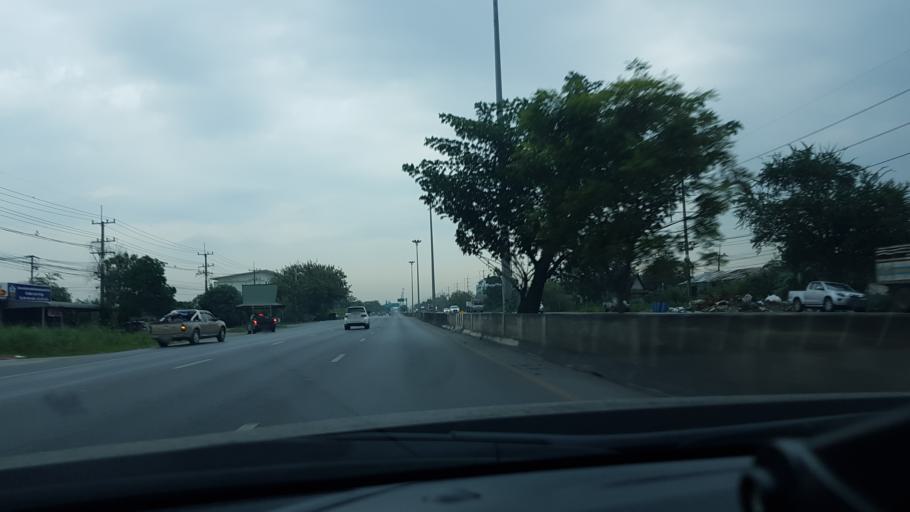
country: TH
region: Pathum Thani
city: Sam Khok
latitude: 14.0894
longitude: 100.5705
